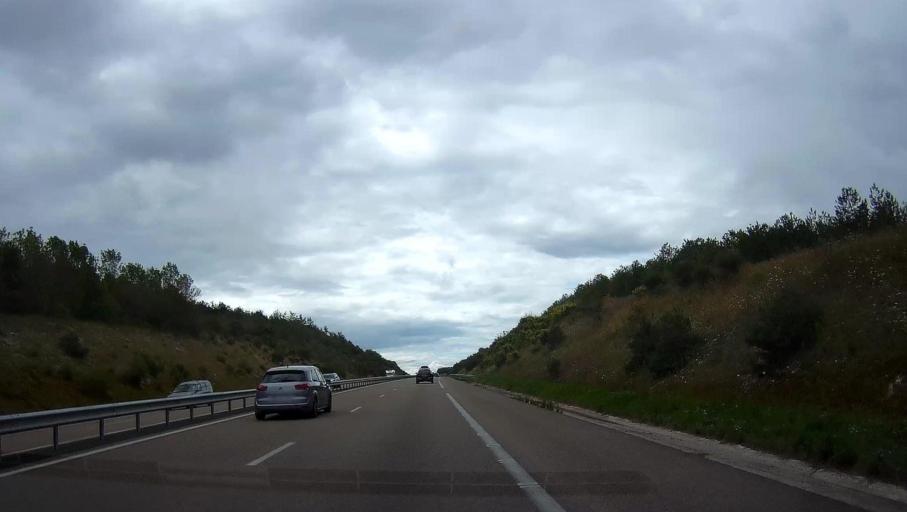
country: FR
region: Champagne-Ardenne
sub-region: Departement de l'Aube
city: Creney-pres-Troyes
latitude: 48.3778
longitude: 4.1572
